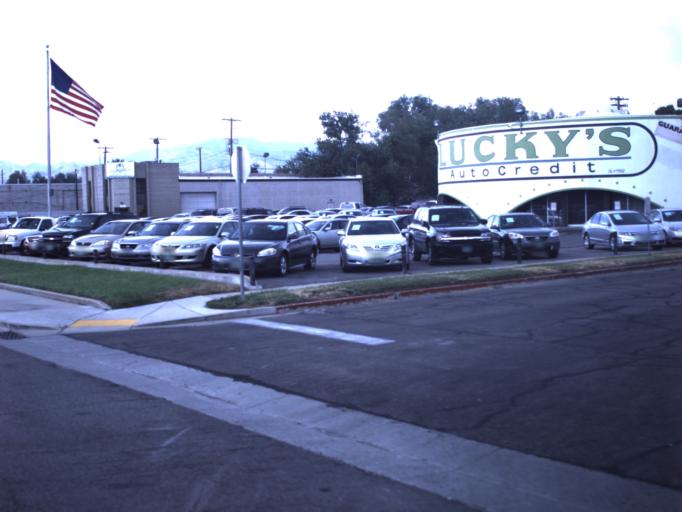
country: US
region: Utah
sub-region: Salt Lake County
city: South Salt Lake
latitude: 40.7035
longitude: -111.8882
